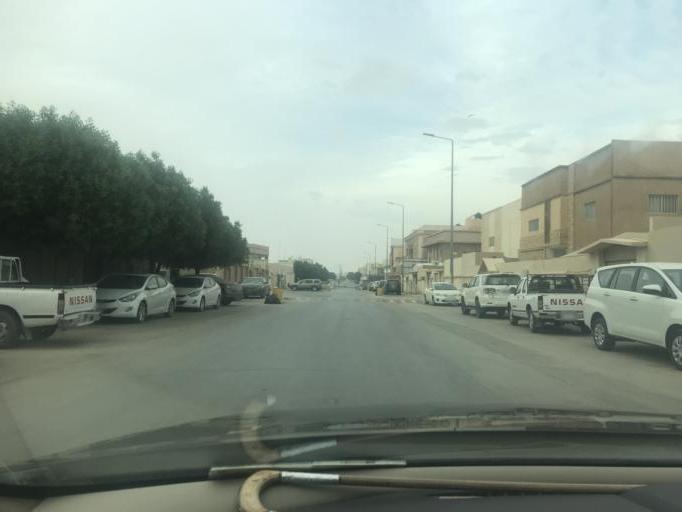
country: SA
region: Ar Riyad
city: Riyadh
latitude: 24.7487
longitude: 46.7701
